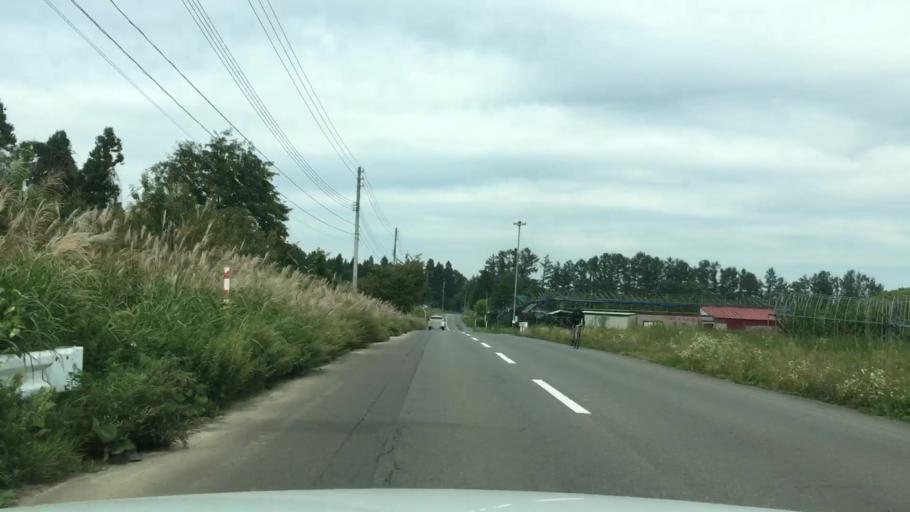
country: JP
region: Aomori
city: Hirosaki
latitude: 40.6788
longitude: 140.3728
